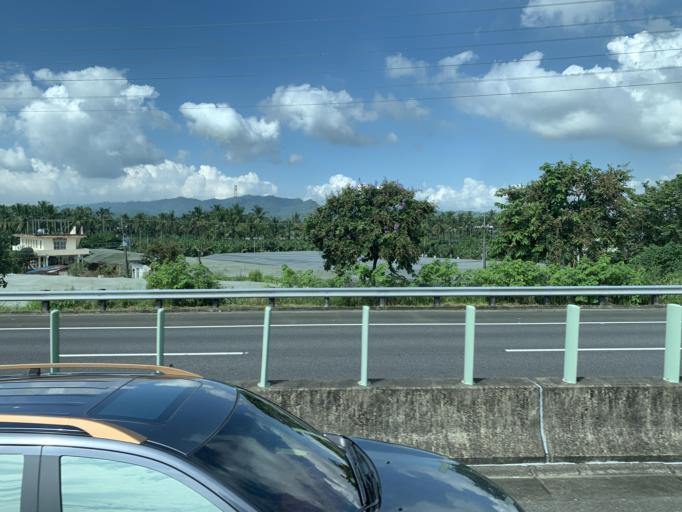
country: TW
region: Taiwan
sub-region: Pingtung
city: Pingtung
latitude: 22.8421
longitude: 120.4960
